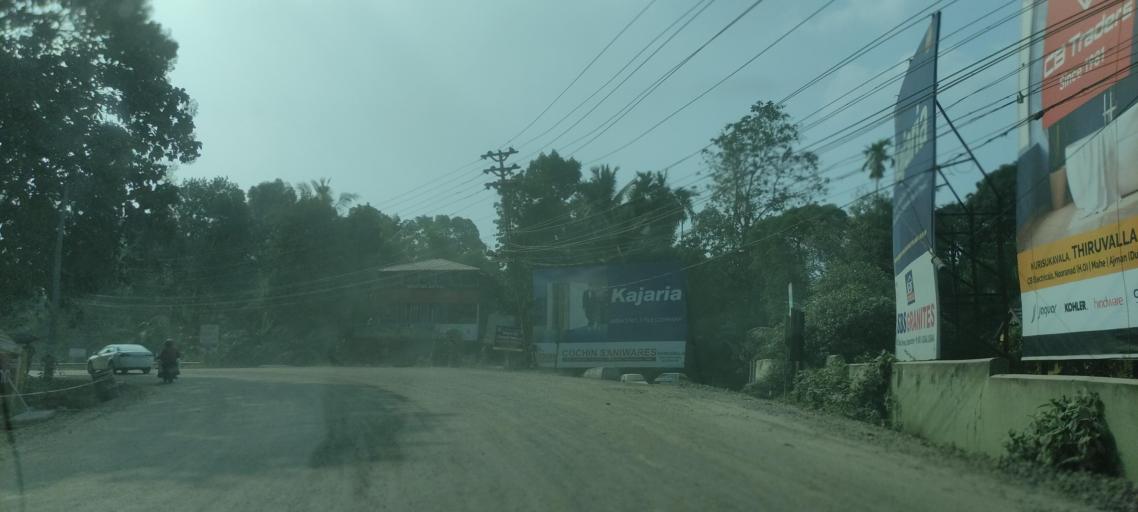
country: IN
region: Kerala
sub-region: Pattanamtitta
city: Tiruvalla
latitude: 9.3742
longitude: 76.5541
